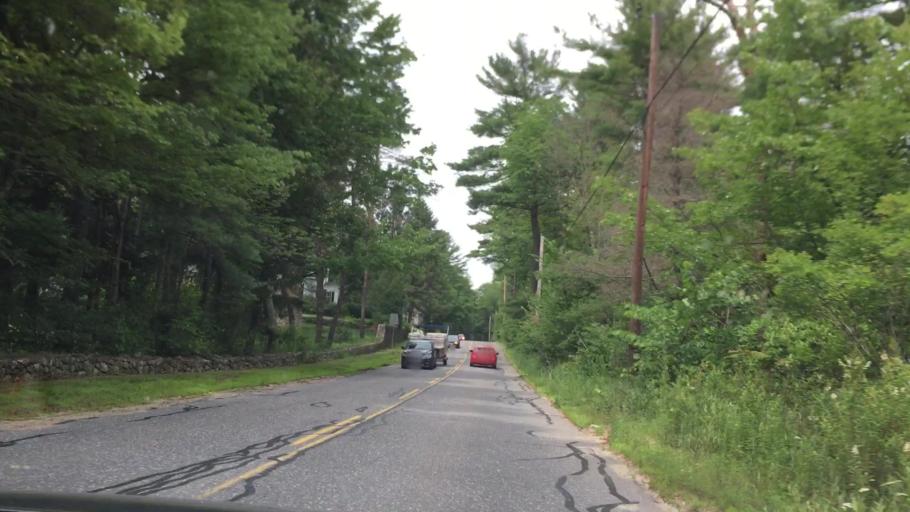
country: US
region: Massachusetts
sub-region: Worcester County
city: Winchendon
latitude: 42.6963
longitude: -72.0150
